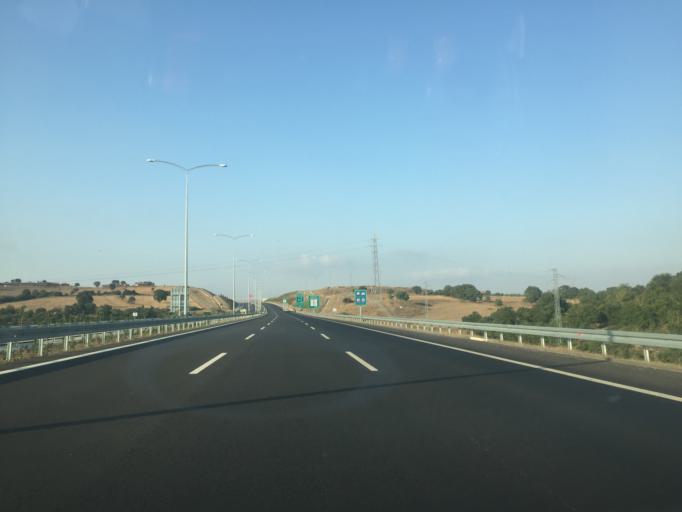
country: TR
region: Balikesir
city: Ertugrul
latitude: 39.6443
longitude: 27.7215
